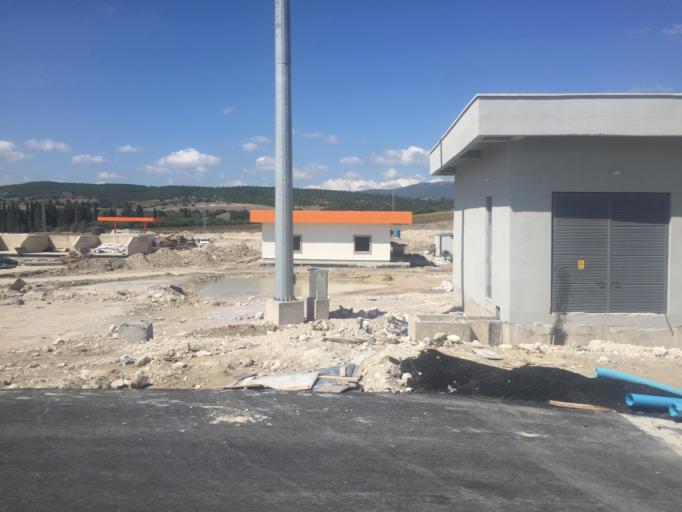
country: TR
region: Balikesir
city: Susurluk
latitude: 39.9613
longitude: 28.1649
